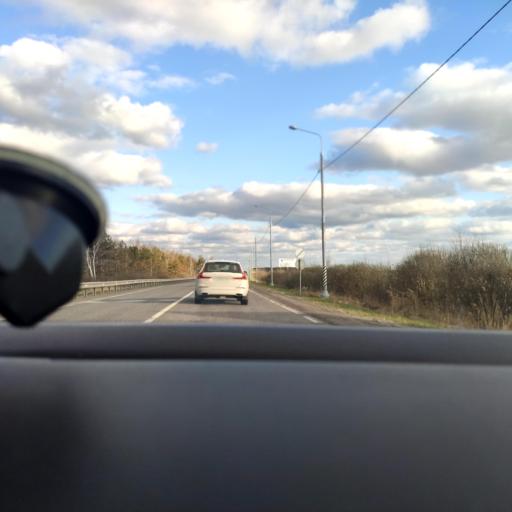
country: RU
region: Moskovskaya
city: Yegor'yevsk
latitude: 55.4444
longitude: 39.0152
